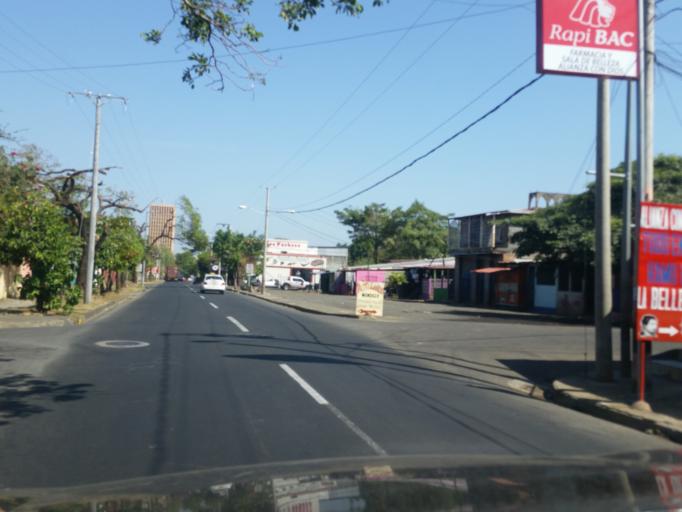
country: NI
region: Managua
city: Managua
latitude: 12.1508
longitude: -86.2795
